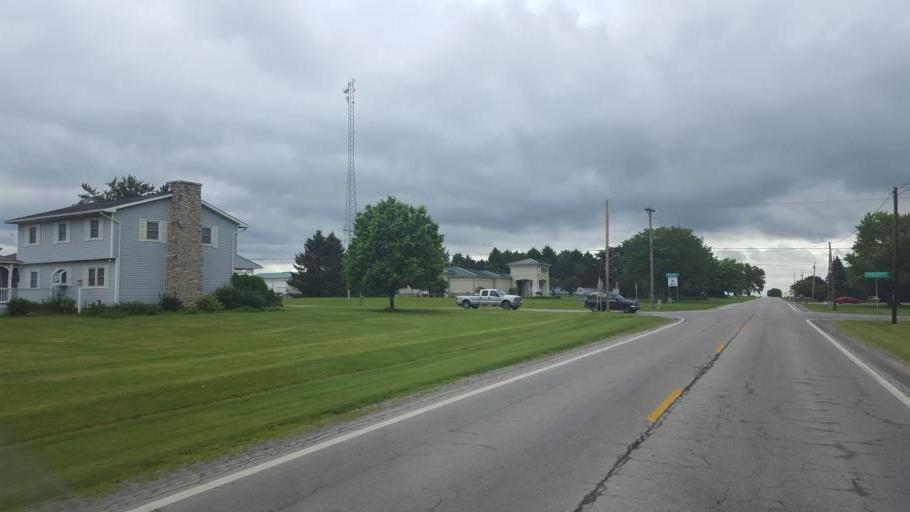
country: US
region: Ohio
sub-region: Marion County
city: Marion
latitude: 40.6440
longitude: -83.1458
